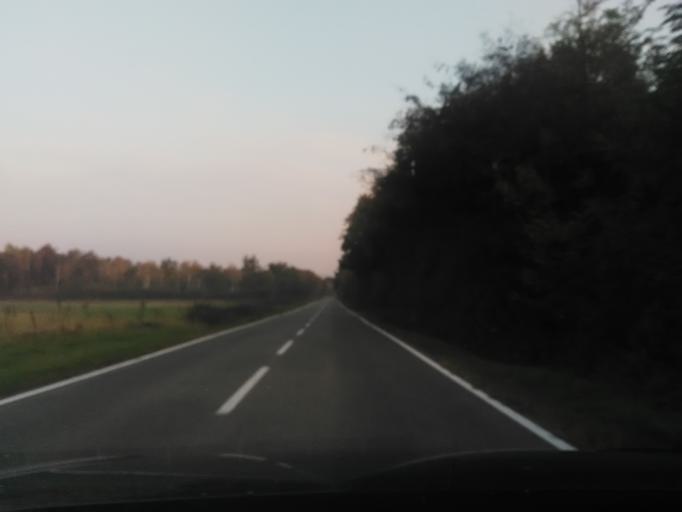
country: IT
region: Piedmont
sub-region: Provincia di Vercelli
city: San Maurizio
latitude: 45.5723
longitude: 8.2950
